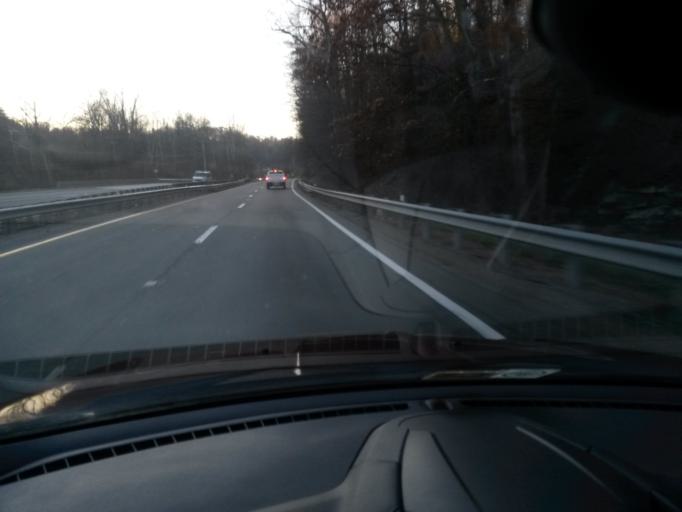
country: US
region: Virginia
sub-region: Roanoke County
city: Narrows
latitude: 37.1260
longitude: -79.9603
